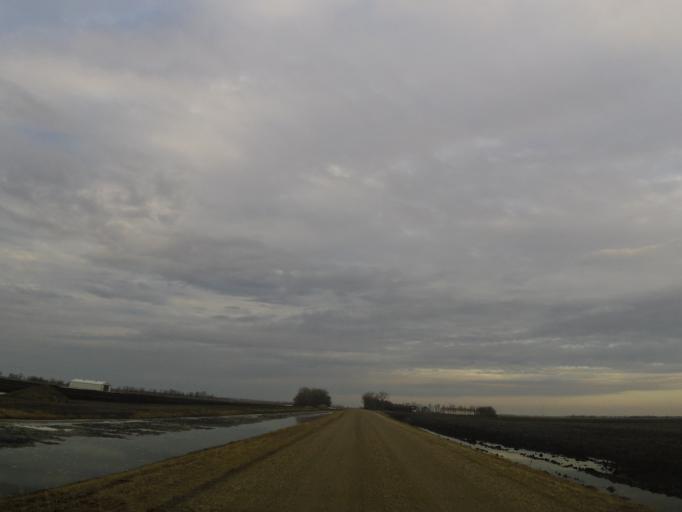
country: US
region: North Dakota
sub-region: Walsh County
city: Grafton
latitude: 48.3686
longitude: -97.2297
